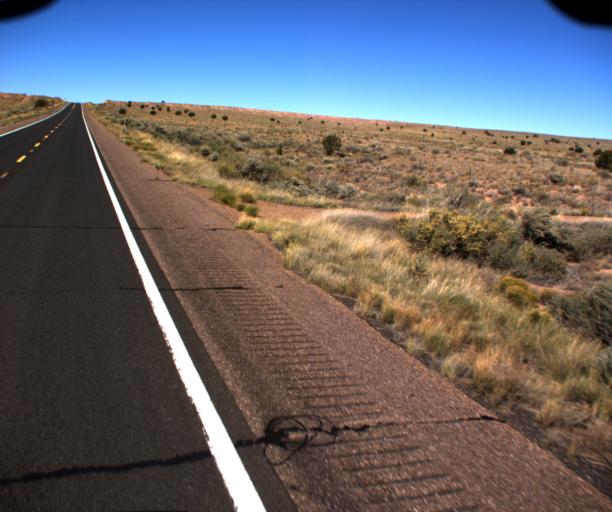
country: US
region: Arizona
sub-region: Navajo County
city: Snowflake
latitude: 34.6831
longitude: -109.7366
